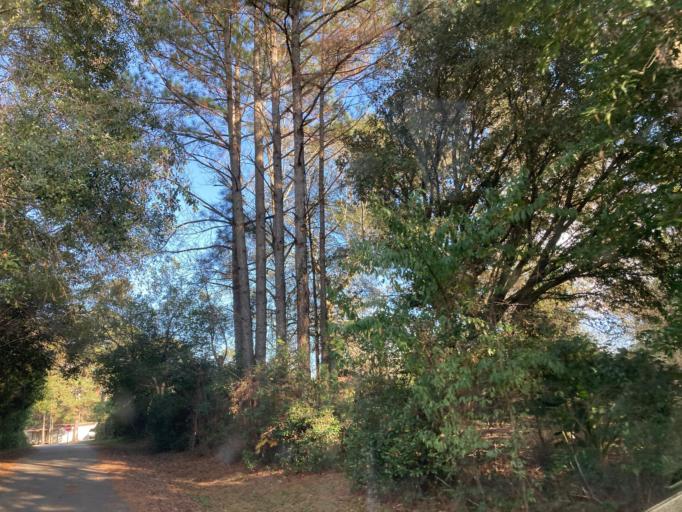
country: US
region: Mississippi
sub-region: Lamar County
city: Sumrall
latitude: 31.3960
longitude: -89.6468
